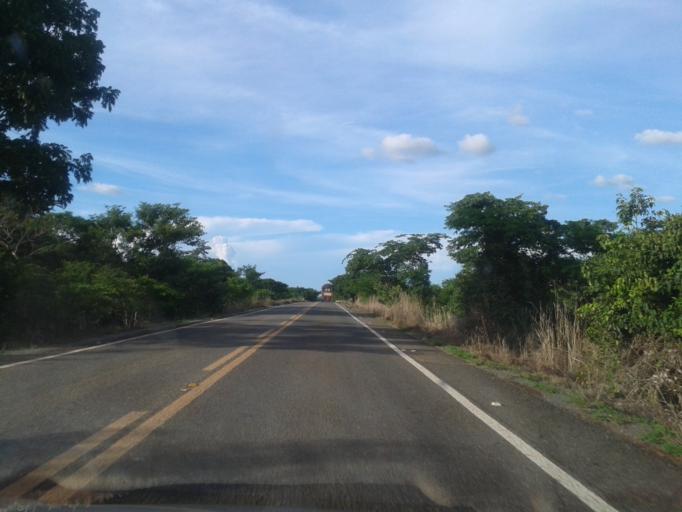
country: BR
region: Goias
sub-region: Sao Miguel Do Araguaia
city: Sao Miguel do Araguaia
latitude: -13.6978
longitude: -50.3319
